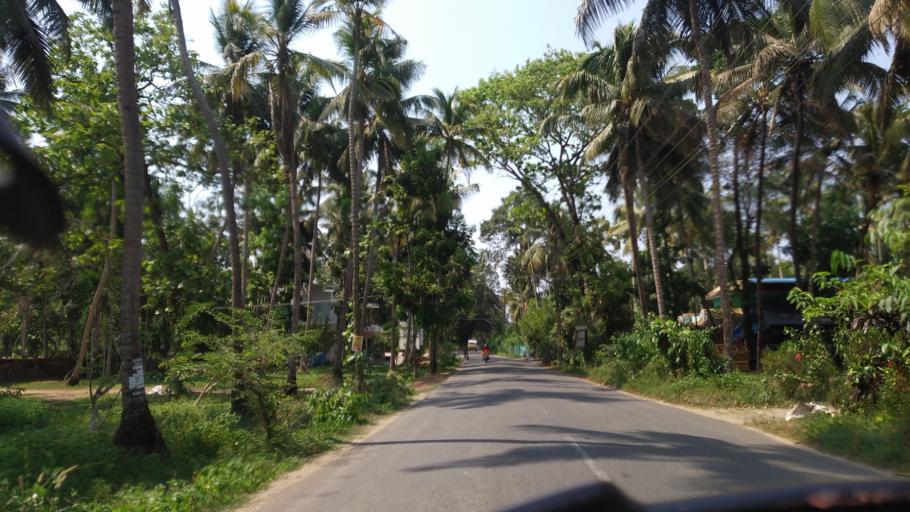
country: IN
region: Kerala
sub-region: Thrissur District
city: Kodungallur
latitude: 10.2702
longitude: 76.1408
